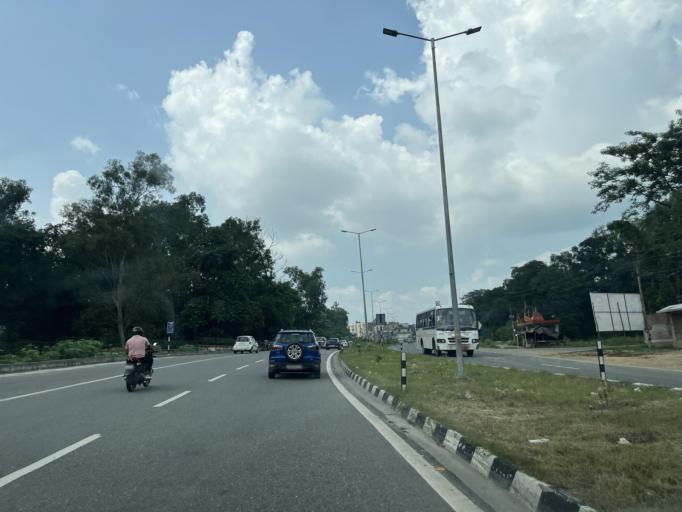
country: IN
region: Uttarakhand
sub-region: Dehradun
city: Raipur
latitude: 30.2670
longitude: 78.0810
